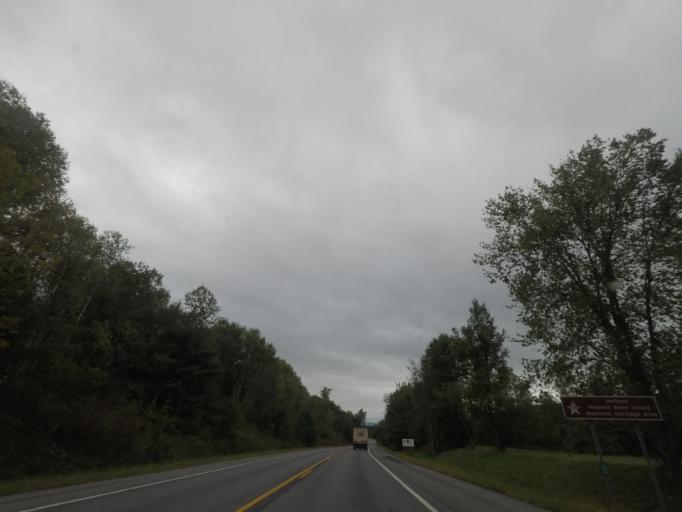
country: US
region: New York
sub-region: Rensselaer County
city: Hoosick Falls
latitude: 42.9414
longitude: -73.3664
